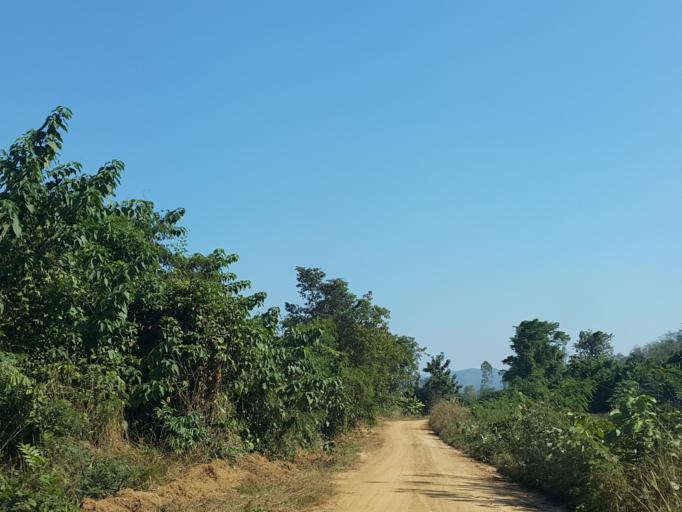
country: TH
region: Sukhothai
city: Thung Saliam
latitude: 17.3165
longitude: 99.4492
